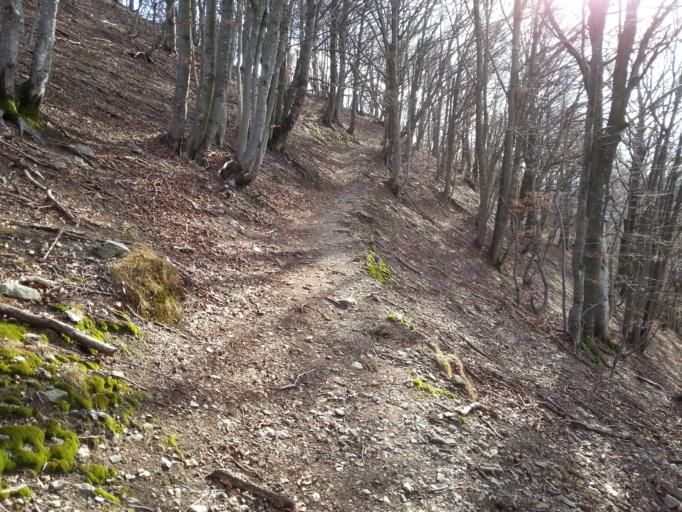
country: CH
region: Ticino
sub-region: Lugano District
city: Gravesano
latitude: 46.0482
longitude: 8.8676
